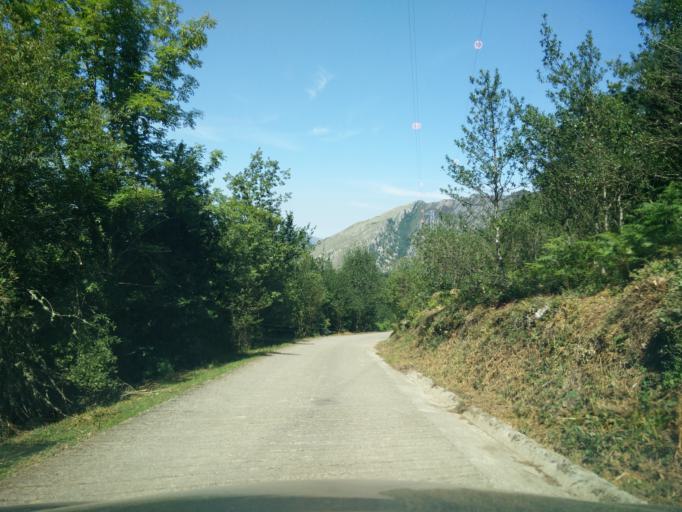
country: ES
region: Asturias
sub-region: Province of Asturias
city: Amieva
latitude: 43.1924
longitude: -5.1460
